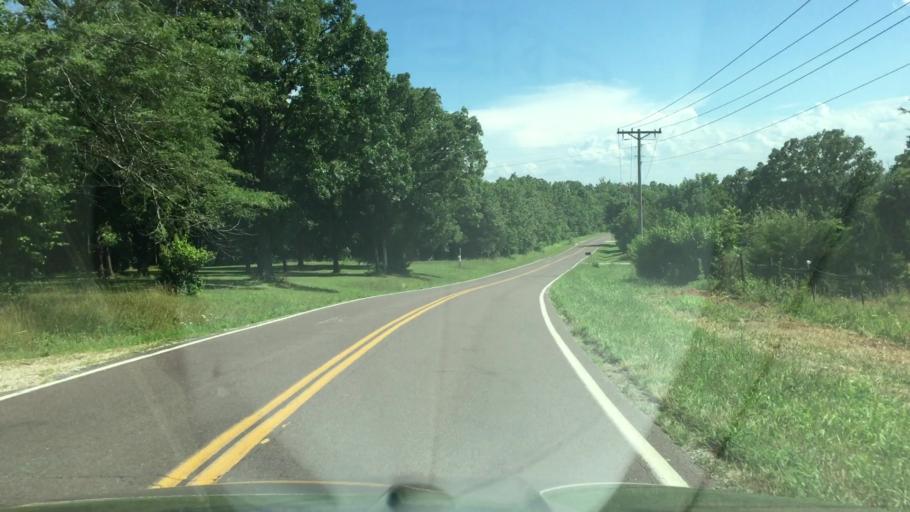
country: US
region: Missouri
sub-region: Miller County
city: Tuscumbia
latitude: 38.1068
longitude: -92.4731
